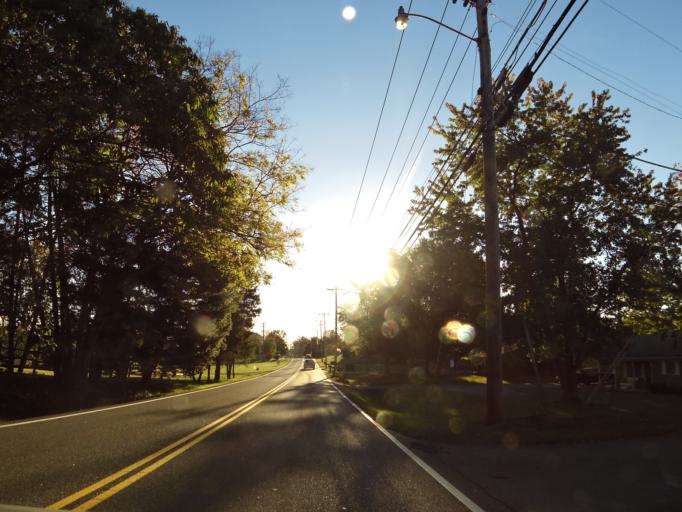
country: US
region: Tennessee
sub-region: Blount County
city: Maryville
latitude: 35.7647
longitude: -83.9416
